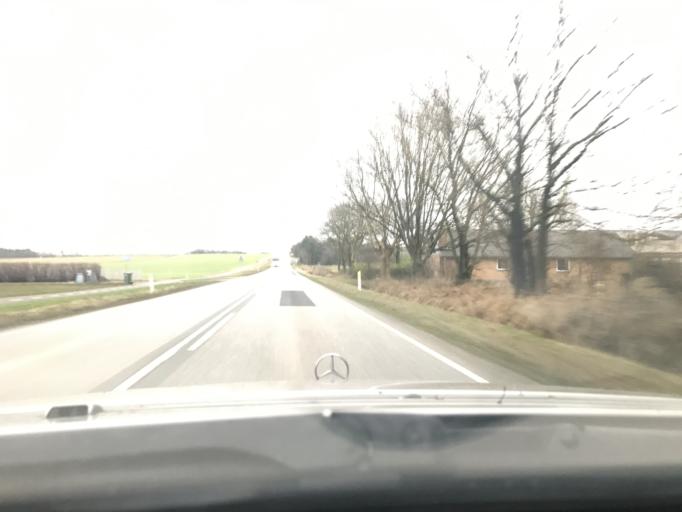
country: DK
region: South Denmark
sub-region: Tonder Kommune
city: Toftlund
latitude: 55.1449
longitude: 9.1151
